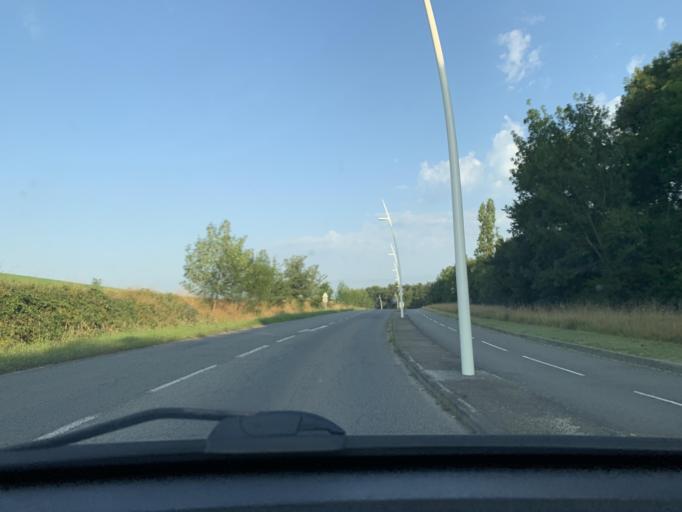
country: FR
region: Midi-Pyrenees
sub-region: Departement de la Haute-Garonne
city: Labege
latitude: 43.5346
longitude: 1.5421
